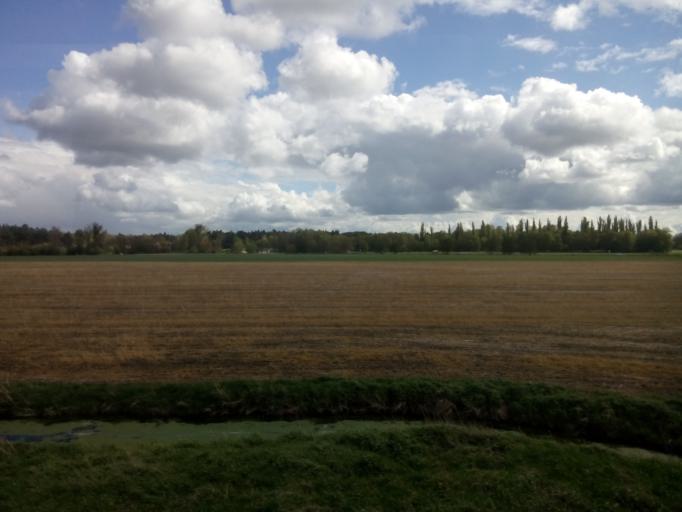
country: DE
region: Brandenburg
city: Falkensee
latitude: 52.6107
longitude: 13.0800
